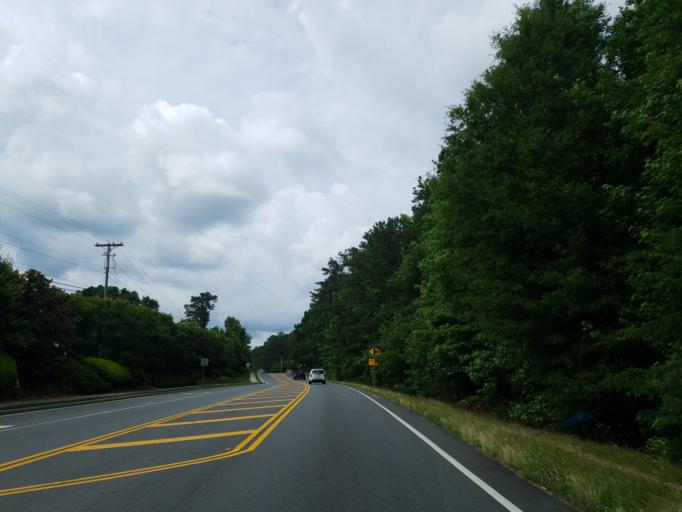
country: US
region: Georgia
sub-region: Fulton County
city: Milton
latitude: 34.1084
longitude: -84.2690
